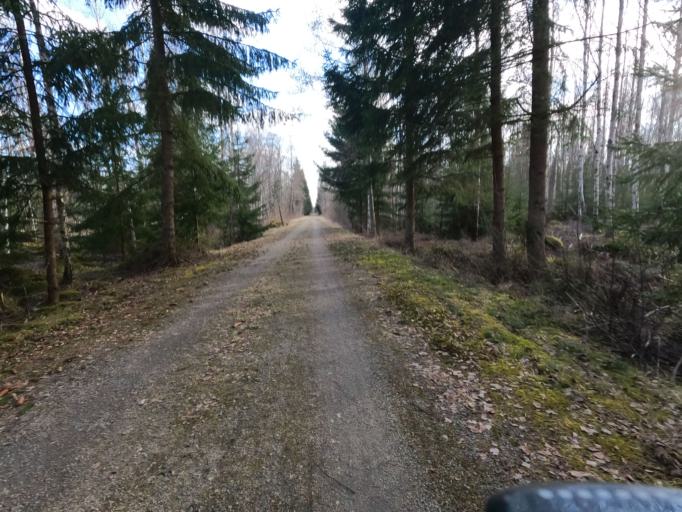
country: SE
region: Kronoberg
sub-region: Alvesta Kommun
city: Vislanda
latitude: 56.6467
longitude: 14.6172
